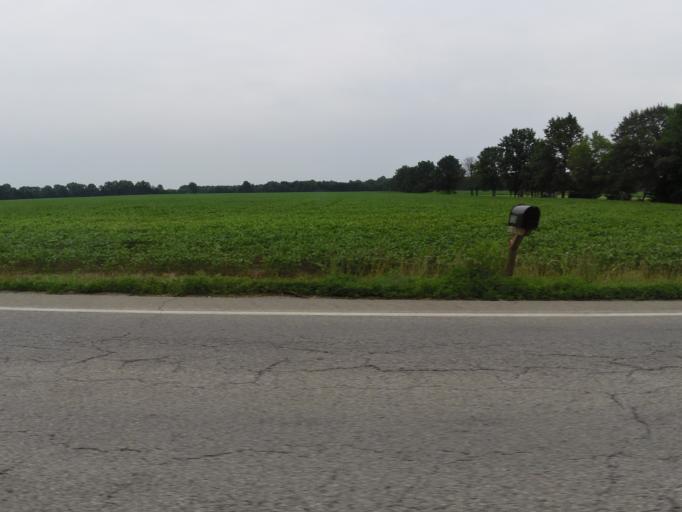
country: US
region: Ohio
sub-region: Brown County
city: Mount Orab
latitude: 39.1522
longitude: -83.9328
